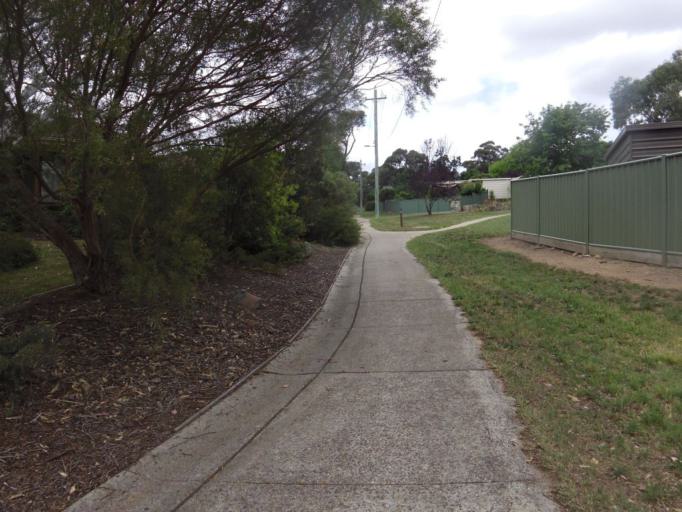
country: AU
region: Australian Capital Territory
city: Macarthur
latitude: -35.4023
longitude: 149.1291
